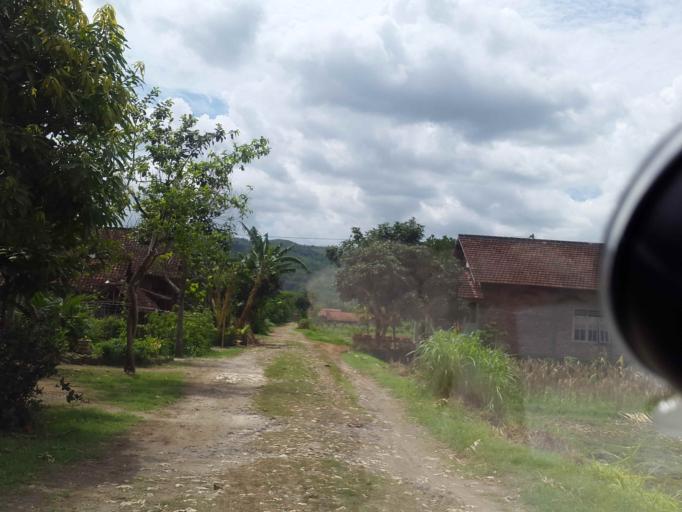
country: ID
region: East Java
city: Pelem
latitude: -8.1519
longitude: 111.8744
